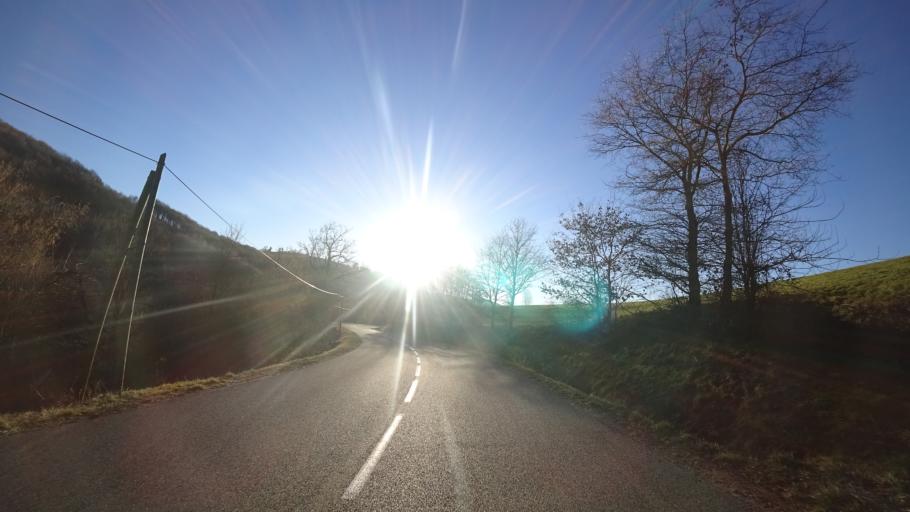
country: FR
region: Midi-Pyrenees
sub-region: Departement de l'Aveyron
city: Pont-de-Salars
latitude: 44.3412
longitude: 2.7333
